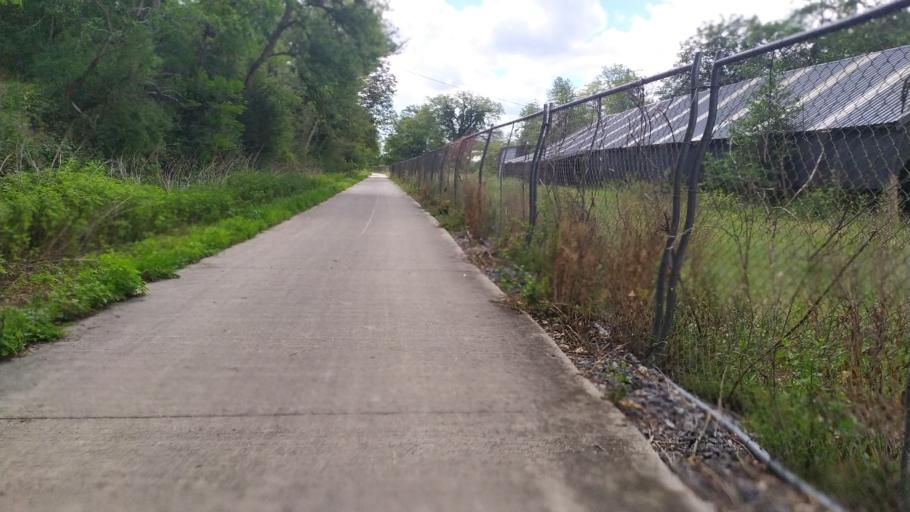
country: BE
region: Wallonia
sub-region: Province du Luxembourg
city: Wellin
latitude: 50.1596
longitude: 5.1160
